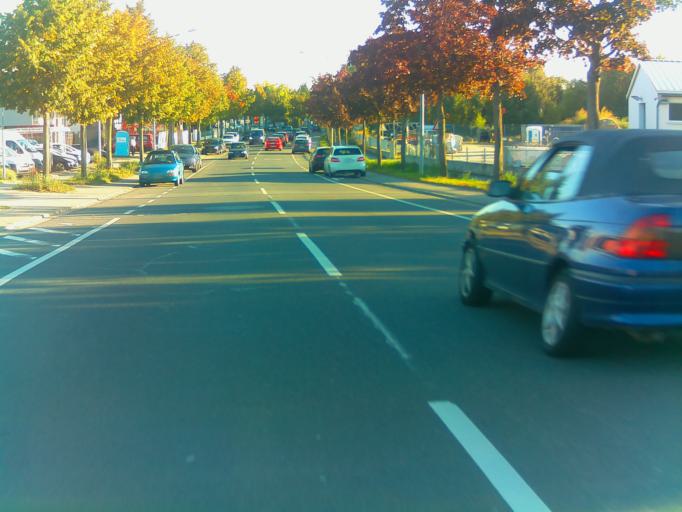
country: DE
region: Hesse
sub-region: Regierungsbezirk Darmstadt
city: Bensheim
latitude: 49.7017
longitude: 8.6101
